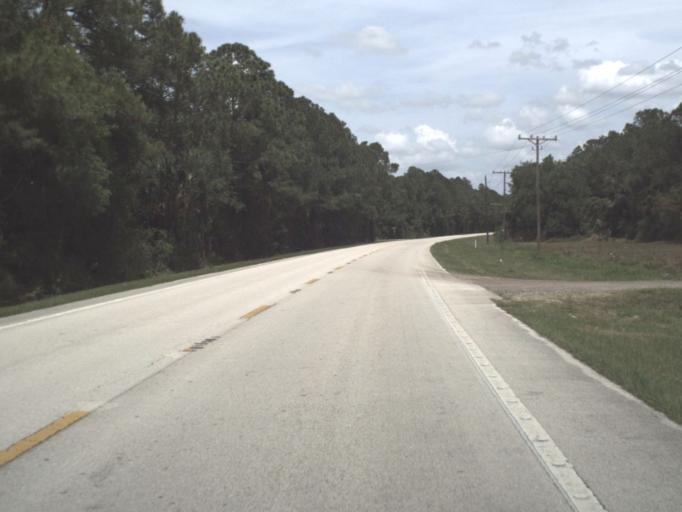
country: US
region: Florida
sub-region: Lake County
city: Lake Mack-Forest Hills
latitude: 28.9980
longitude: -81.3933
